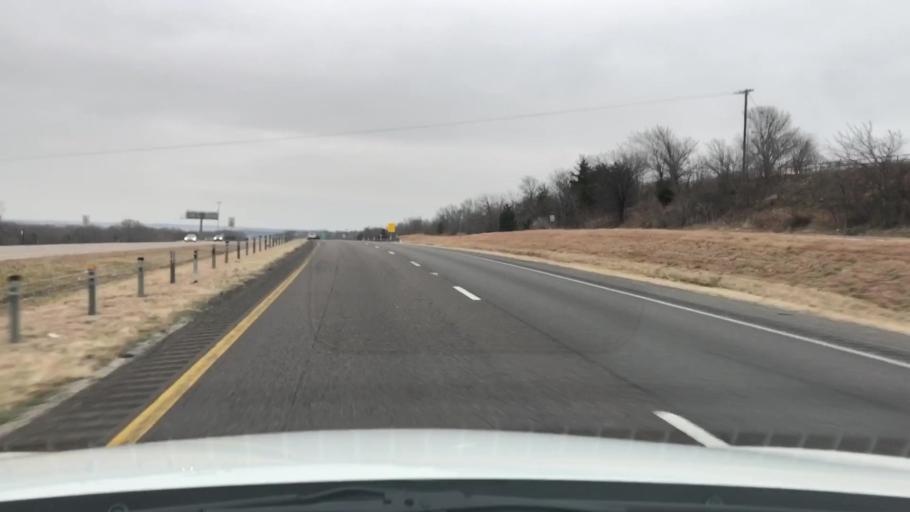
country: US
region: Texas
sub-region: Cooke County
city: Gainesville
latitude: 33.7091
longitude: -97.1616
